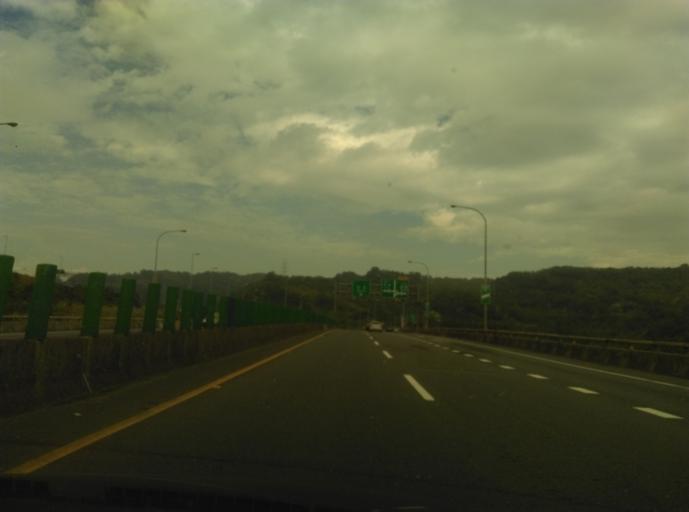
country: TW
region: Taiwan
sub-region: Keelung
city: Keelung
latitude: 25.1219
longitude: 121.6979
